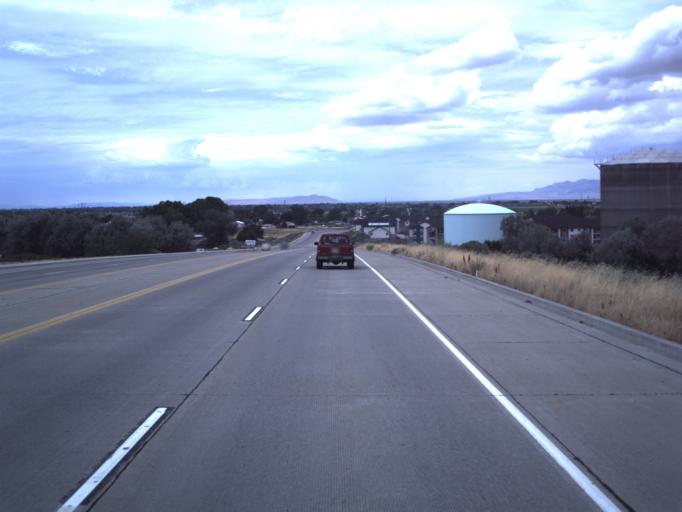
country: US
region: Utah
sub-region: Weber County
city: West Haven
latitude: 41.1978
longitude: -112.0299
